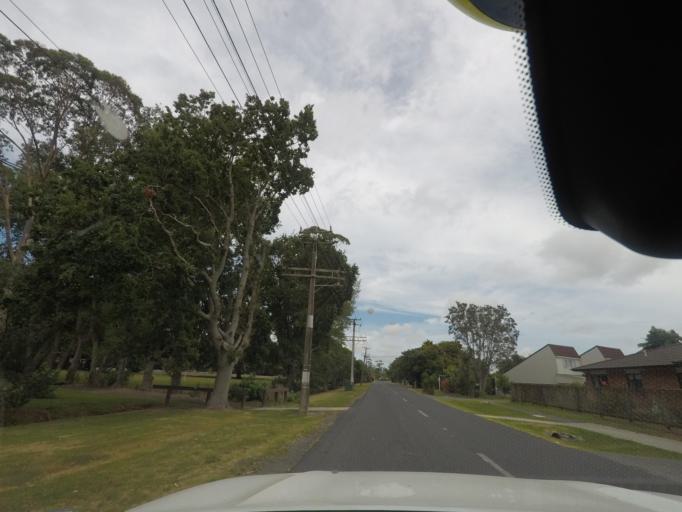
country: NZ
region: Auckland
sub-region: Auckland
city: Parakai
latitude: -36.6582
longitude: 174.4338
